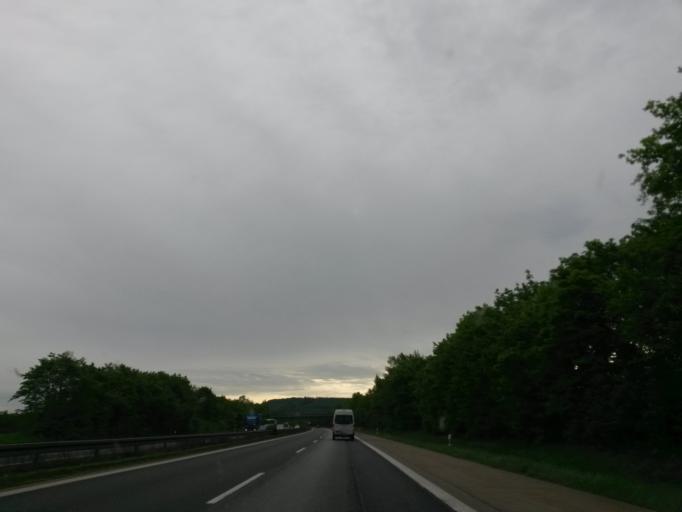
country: DE
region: Bavaria
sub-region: Regierungsbezirk Unterfranken
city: Castell
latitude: 49.7738
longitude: 10.3737
